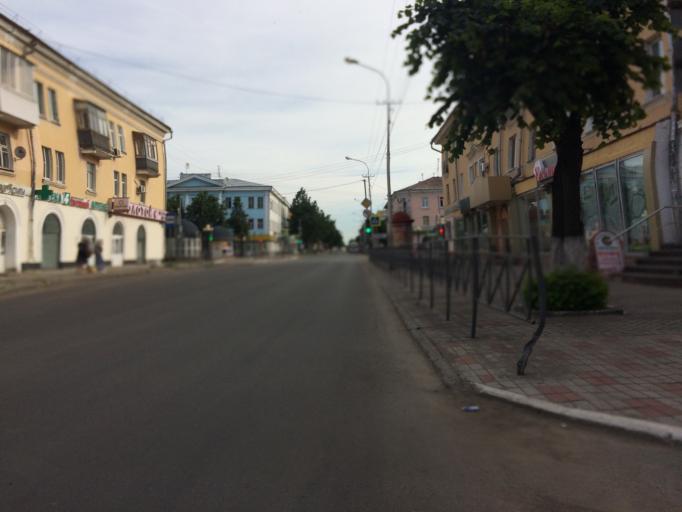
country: RU
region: Mariy-El
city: Yoshkar-Ola
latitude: 56.6342
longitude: 47.8970
